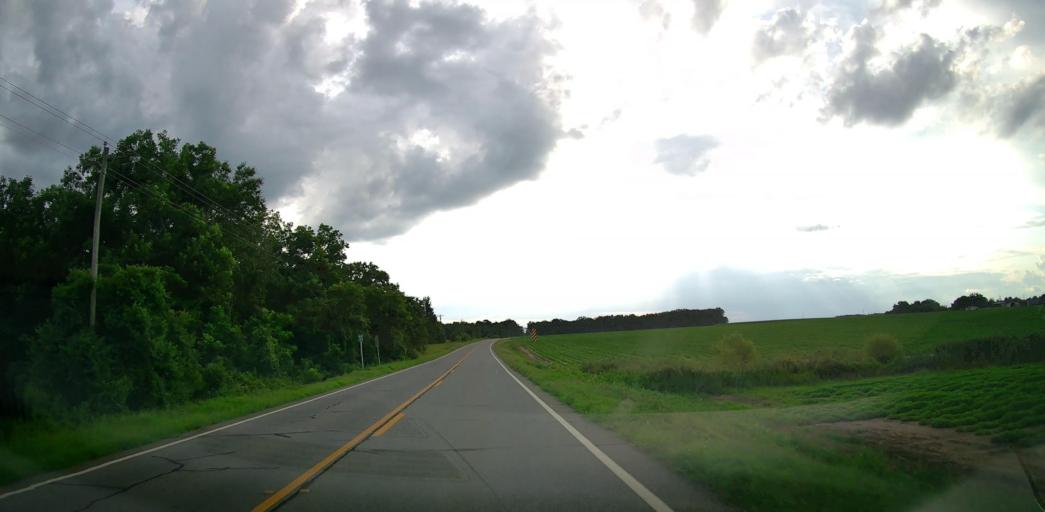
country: US
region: Georgia
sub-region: Pulaski County
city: Hawkinsville
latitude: 32.2957
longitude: -83.5402
